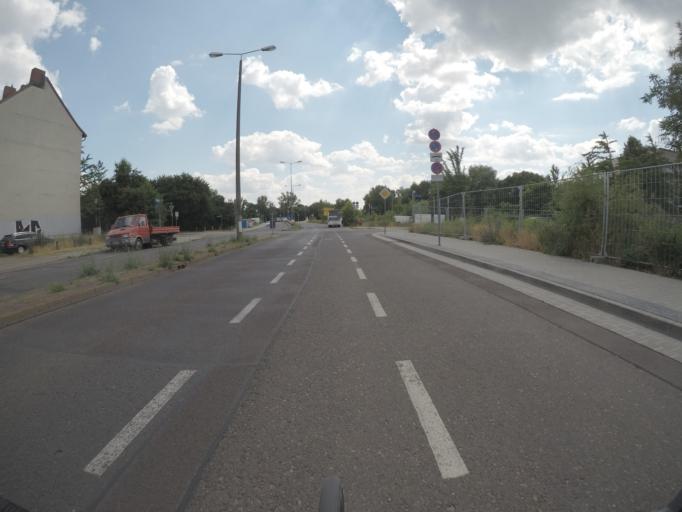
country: DE
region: Brandenburg
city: Brandenburg an der Havel
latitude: 52.4014
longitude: 12.5590
